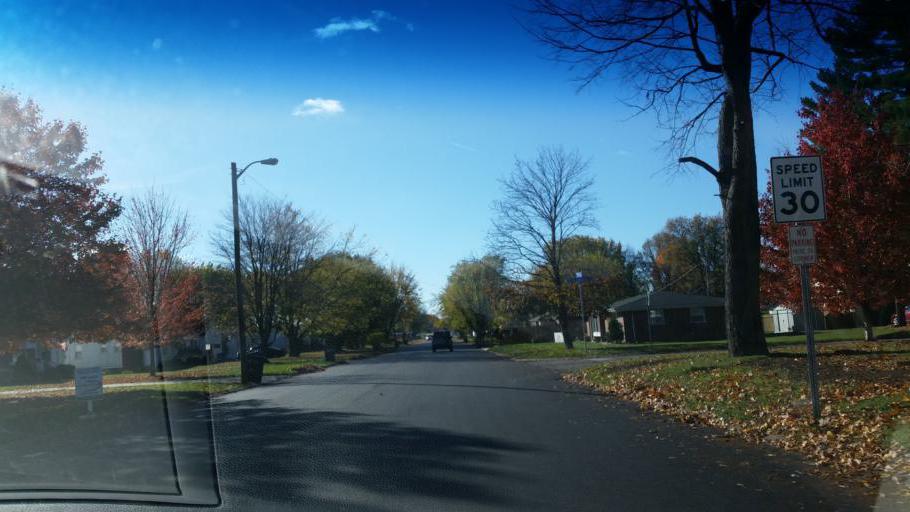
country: US
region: Indiana
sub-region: Howard County
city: Kokomo
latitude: 40.4585
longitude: -86.1365
